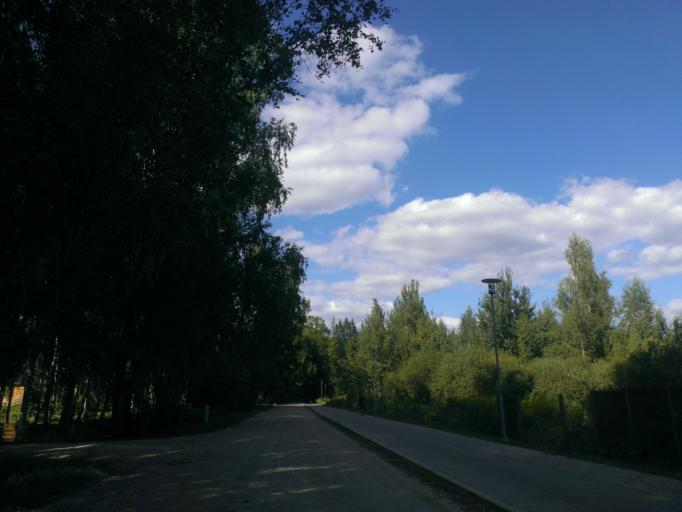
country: LV
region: Sigulda
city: Sigulda
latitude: 57.1685
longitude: 24.8713
